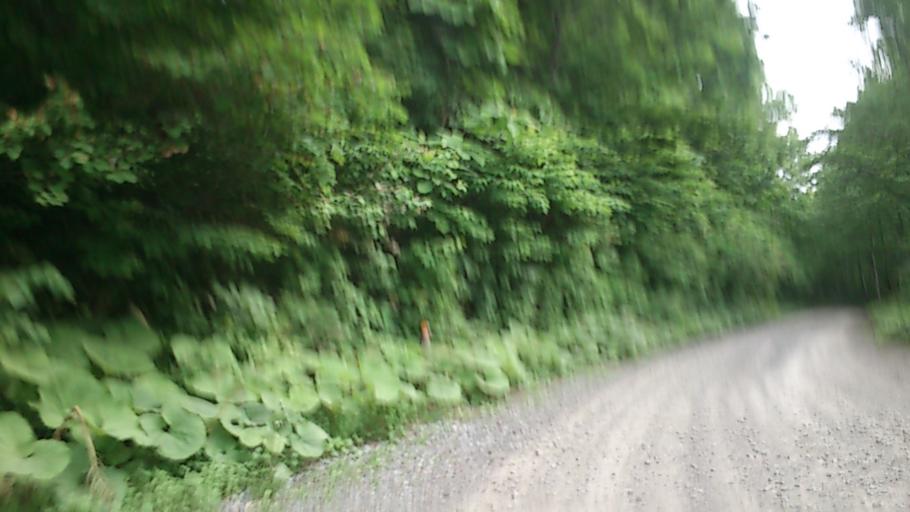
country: JP
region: Aomori
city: Hirosaki
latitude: 40.5589
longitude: 140.1836
